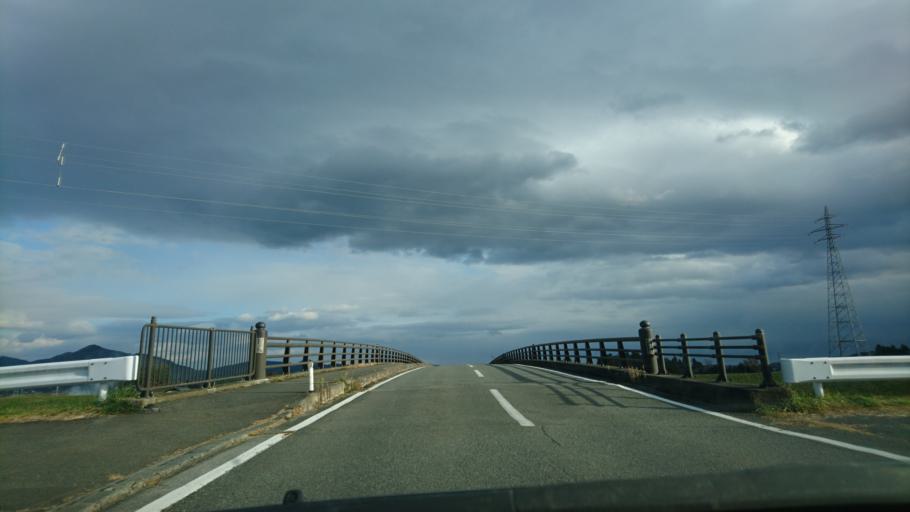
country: JP
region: Iwate
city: Ichinoseki
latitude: 38.9811
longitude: 141.1116
